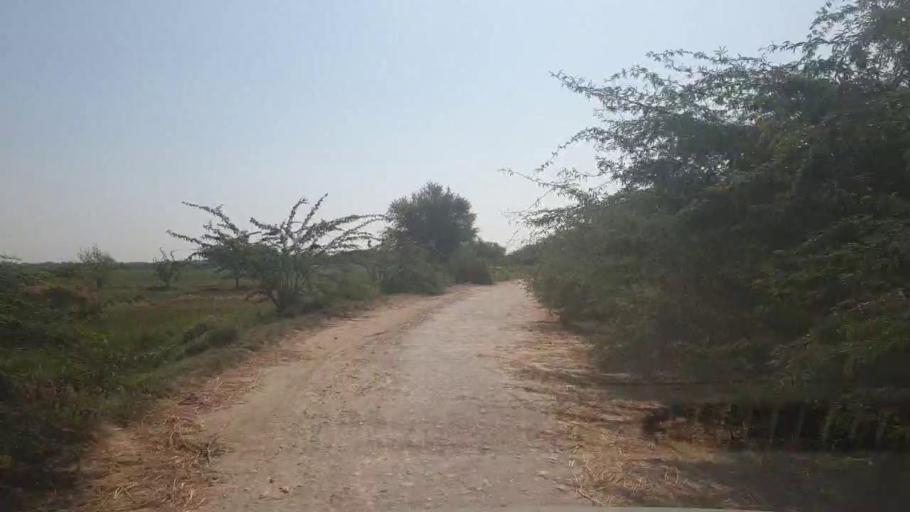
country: PK
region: Sindh
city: Badin
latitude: 24.6565
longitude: 68.9196
